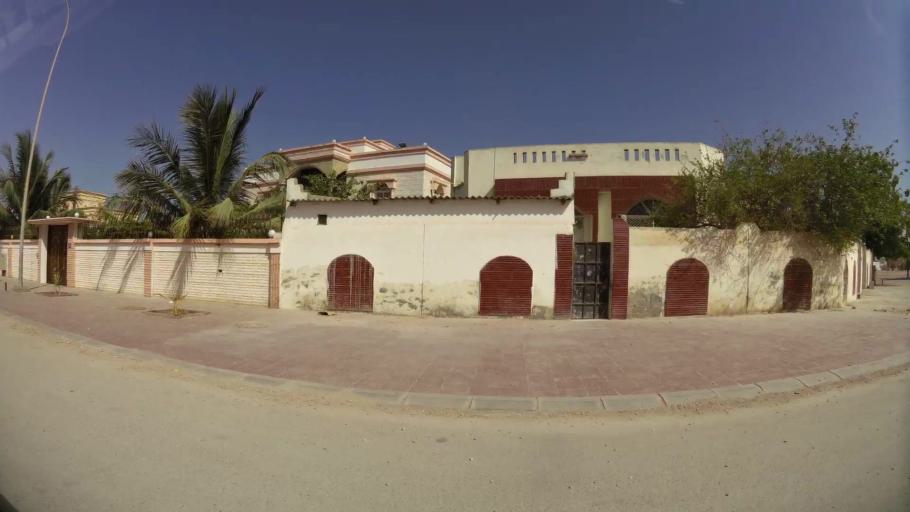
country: OM
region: Zufar
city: Salalah
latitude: 17.0016
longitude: 54.0097
